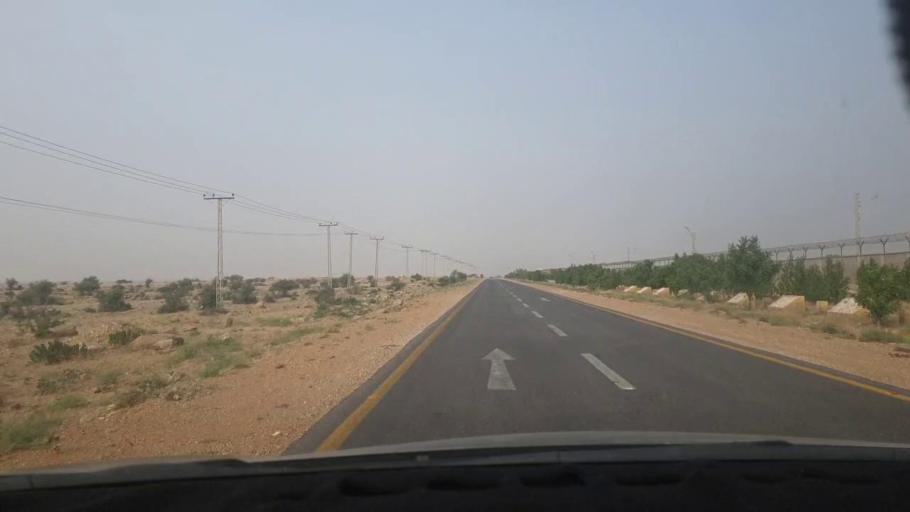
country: PK
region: Sindh
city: Jamshoro
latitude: 25.5460
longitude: 68.3202
